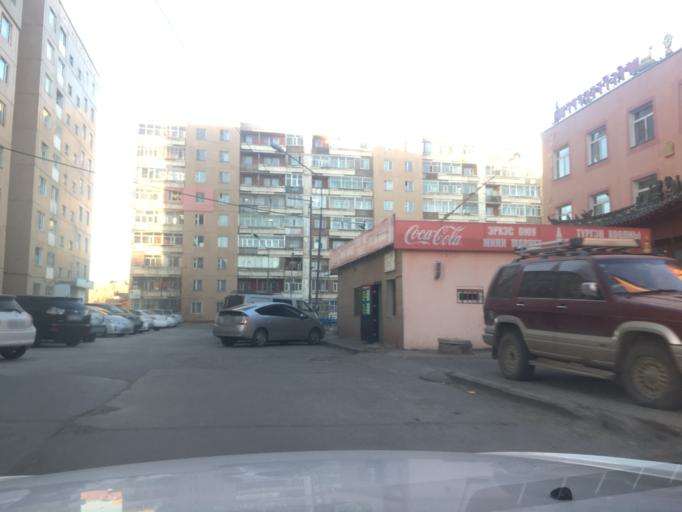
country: MN
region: Ulaanbaatar
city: Ulaanbaatar
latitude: 47.9142
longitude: 106.8318
